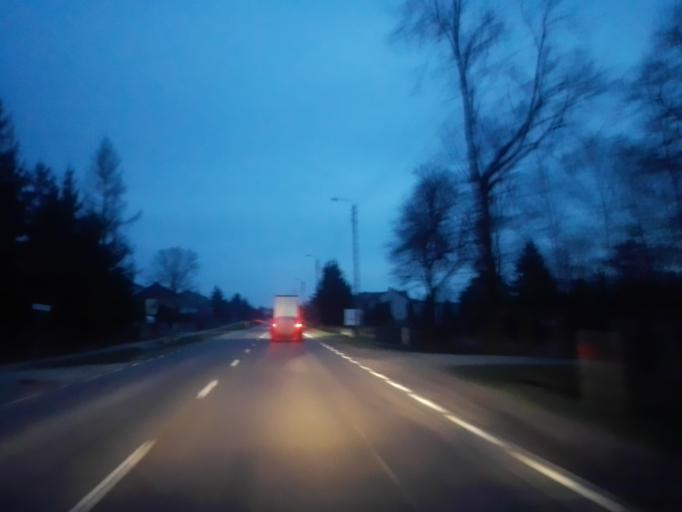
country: PL
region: Podlasie
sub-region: Lomza
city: Lomza
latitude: 53.1323
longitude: 22.0408
